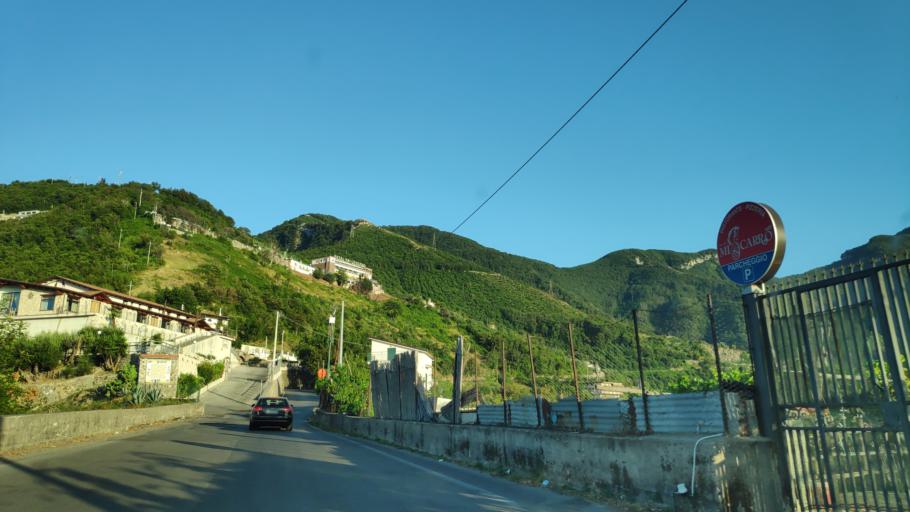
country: IT
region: Campania
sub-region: Provincia di Salerno
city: Corbara
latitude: 40.7270
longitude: 14.5975
